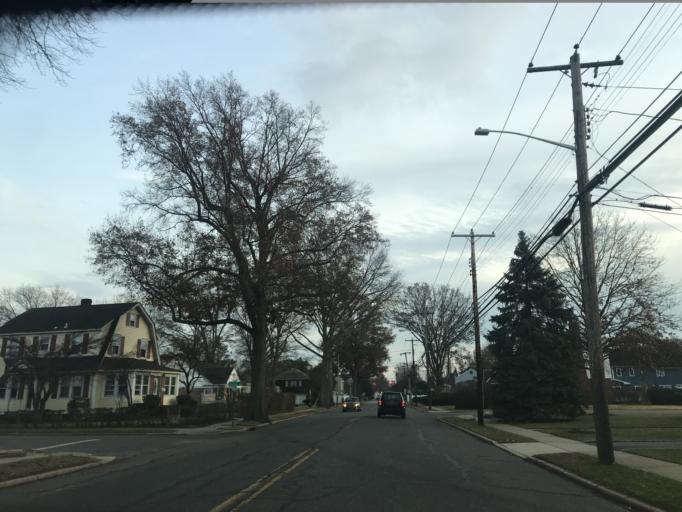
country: US
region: New York
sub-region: Nassau County
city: Westbury
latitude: 40.7553
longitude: -73.5981
